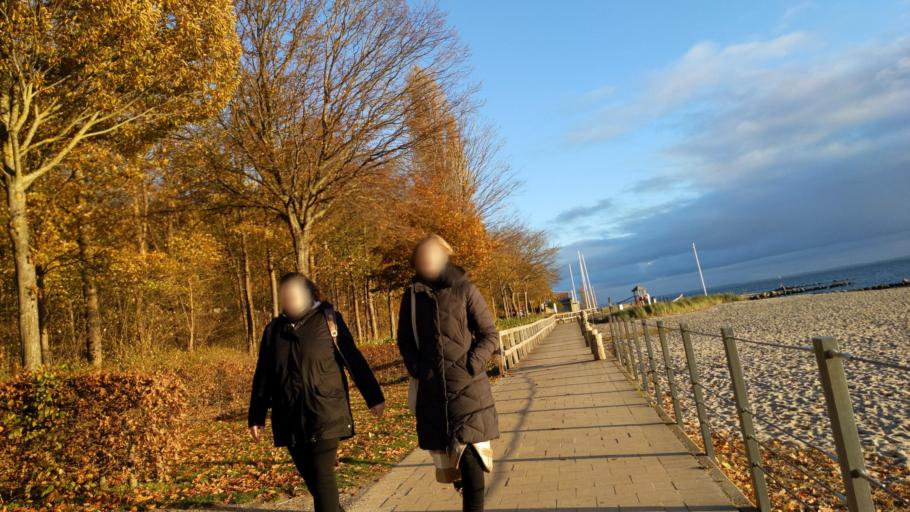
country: DE
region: Schleswig-Holstein
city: Neustadt in Holstein
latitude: 54.0926
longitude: 10.8158
